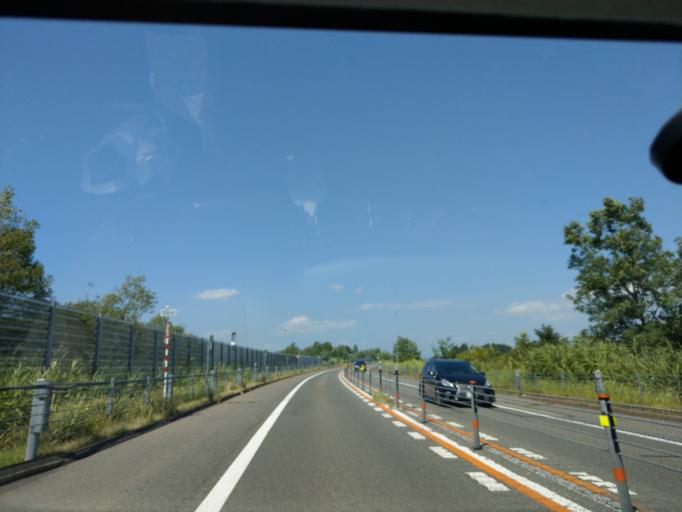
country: JP
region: Akita
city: Yokotemachi
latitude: 39.3472
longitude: 140.4980
